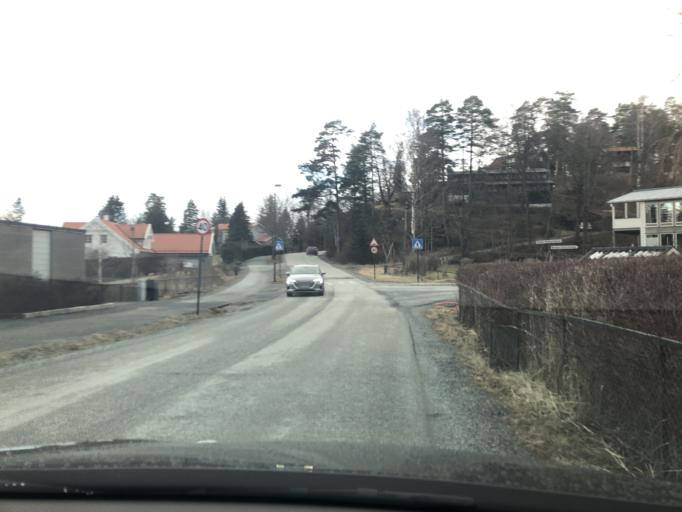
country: NO
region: Akershus
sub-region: Baerum
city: Sandvika
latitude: 59.8604
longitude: 10.5162
